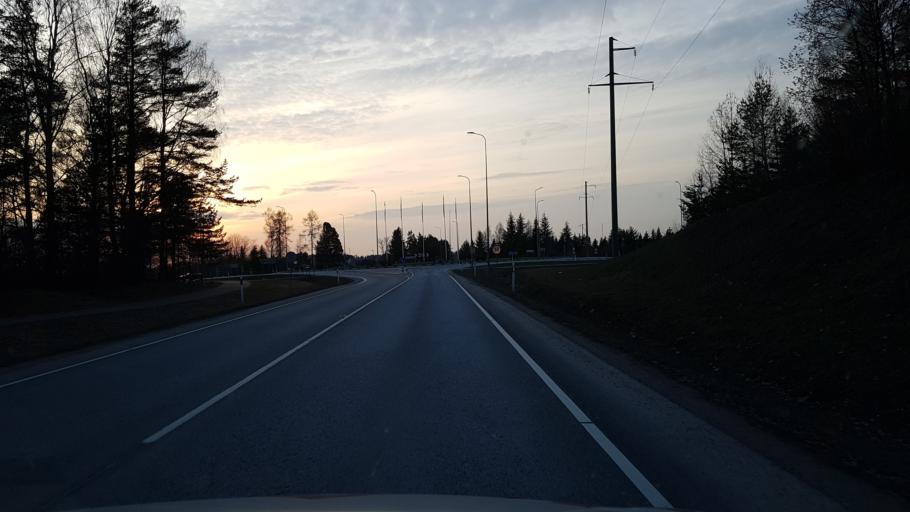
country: EE
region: Laeaene-Virumaa
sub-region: Rakvere linn
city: Rakvere
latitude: 59.3254
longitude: 26.3515
